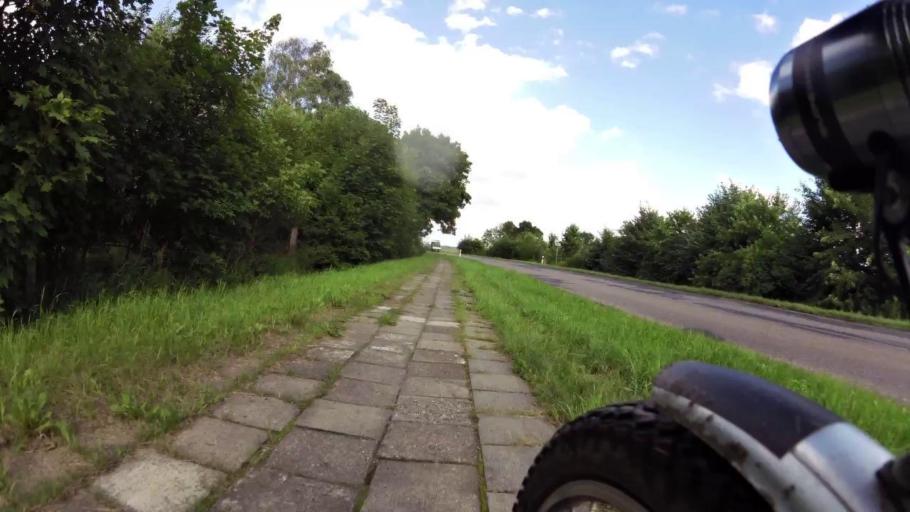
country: PL
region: West Pomeranian Voivodeship
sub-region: Powiat swidwinski
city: Swidwin
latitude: 53.7755
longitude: 15.8401
